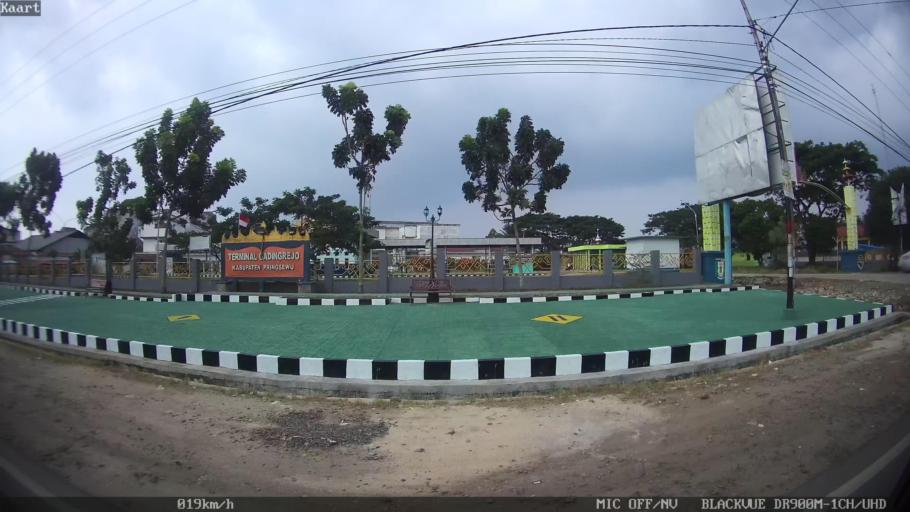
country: ID
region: Lampung
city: Gadingrejo
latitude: -5.3742
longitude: 105.0613
